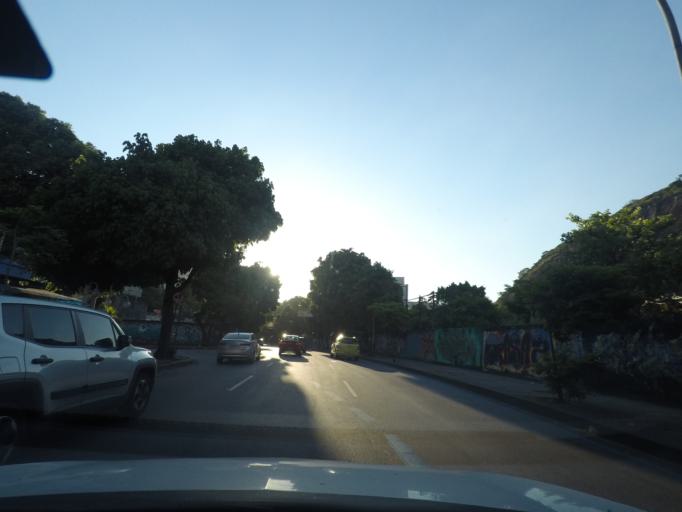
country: BR
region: Rio de Janeiro
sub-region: Rio De Janeiro
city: Rio de Janeiro
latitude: -22.9209
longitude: -43.2264
